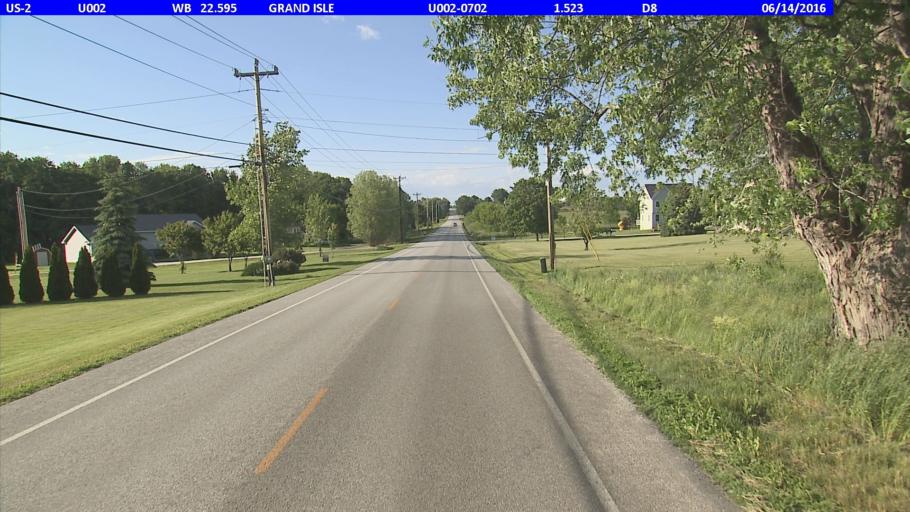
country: US
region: Vermont
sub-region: Grand Isle County
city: North Hero
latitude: 44.7455
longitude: -73.2886
